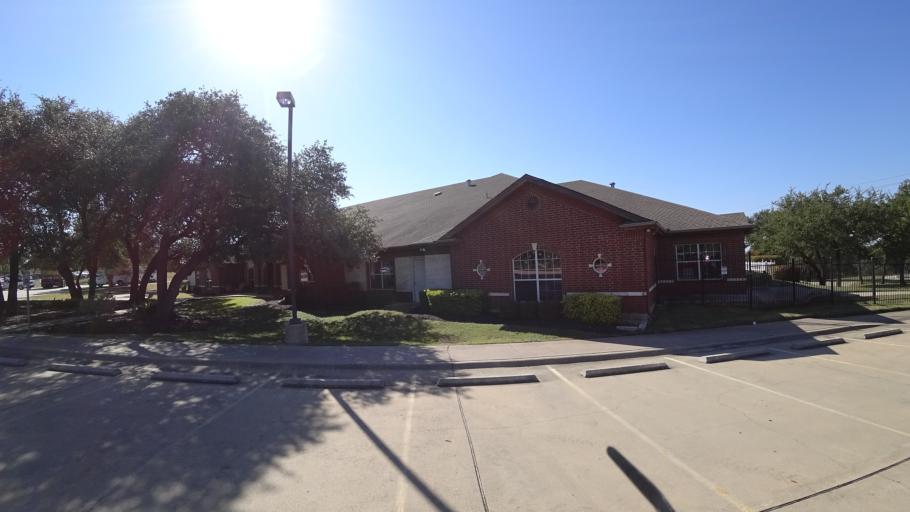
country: US
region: Texas
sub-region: Williamson County
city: Anderson Mill
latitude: 30.3909
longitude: -97.8466
